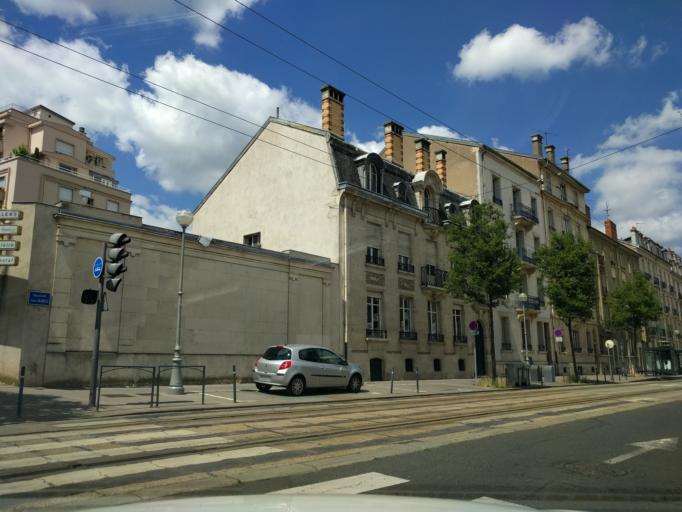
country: FR
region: Lorraine
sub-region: Departement de Meurthe-et-Moselle
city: Nancy
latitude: 48.6807
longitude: 6.1789
